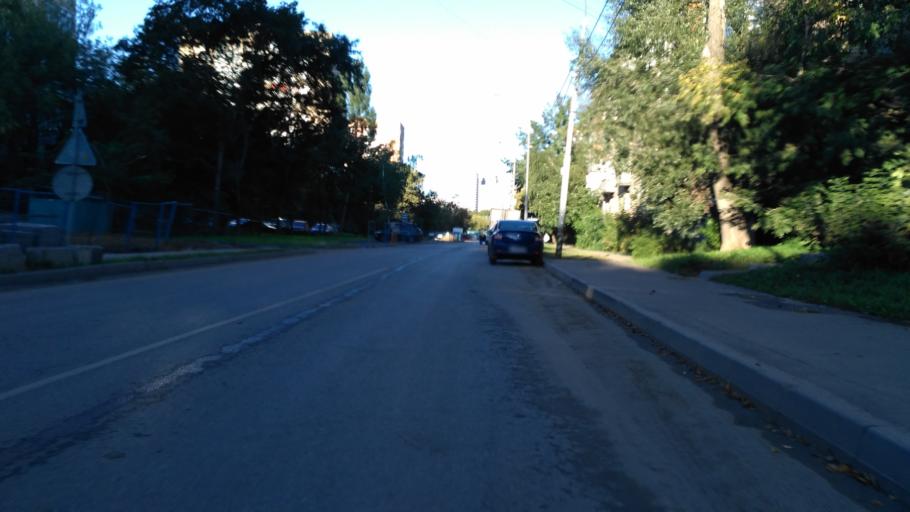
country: RU
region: Moscow
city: Novovladykino
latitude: 55.8301
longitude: 37.5927
